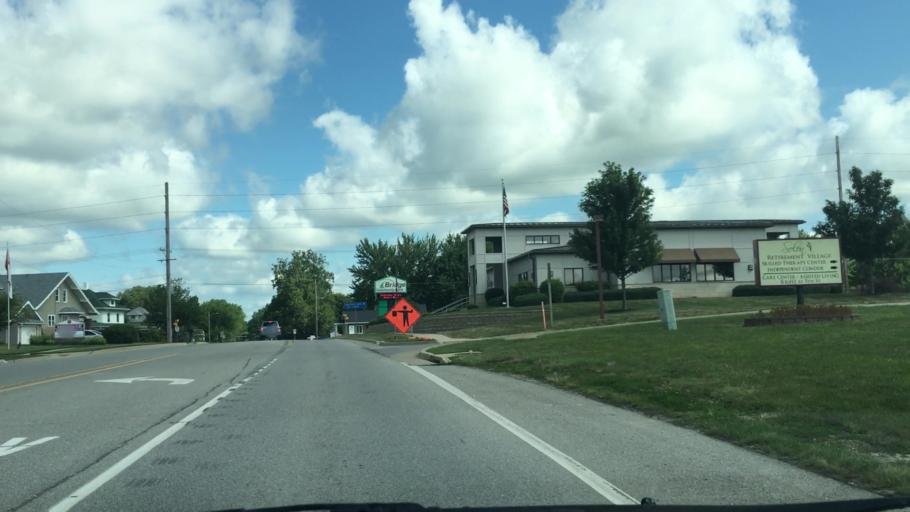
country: US
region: Iowa
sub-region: Johnson County
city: Solon
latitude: 41.8010
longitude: -91.4913
